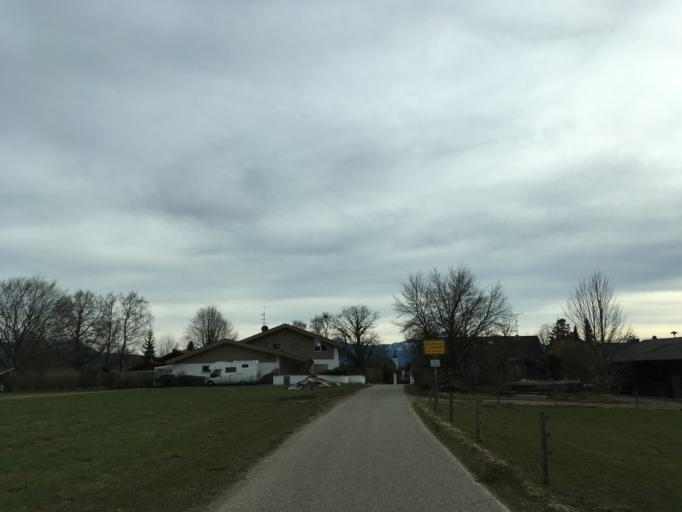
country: DE
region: Bavaria
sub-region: Upper Bavaria
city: Gstadt am Chiemsee
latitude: 47.8941
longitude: 12.4010
